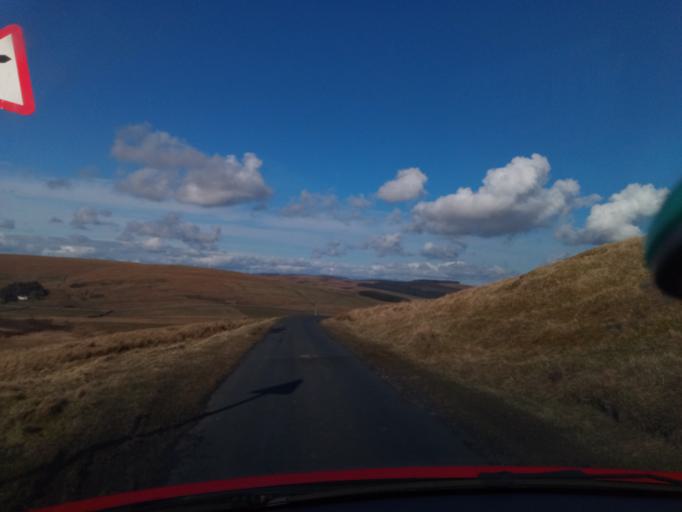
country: GB
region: Scotland
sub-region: The Scottish Borders
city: Hawick
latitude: 55.4463
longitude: -2.8877
